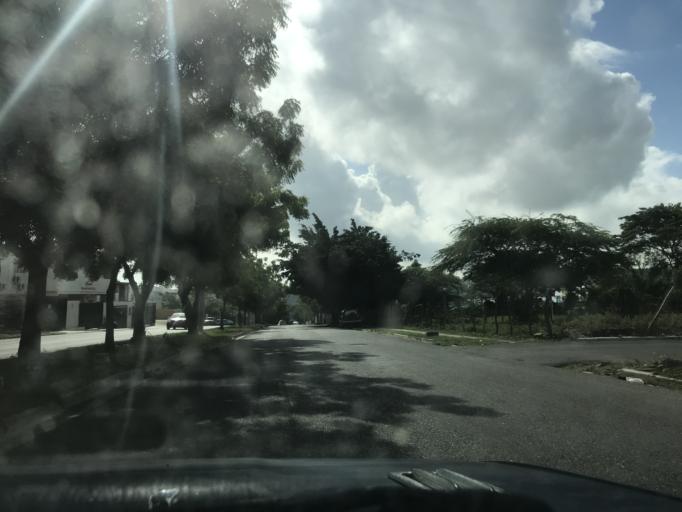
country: DO
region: Santiago
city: Santiago de los Caballeros
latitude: 19.4139
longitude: -70.7221
